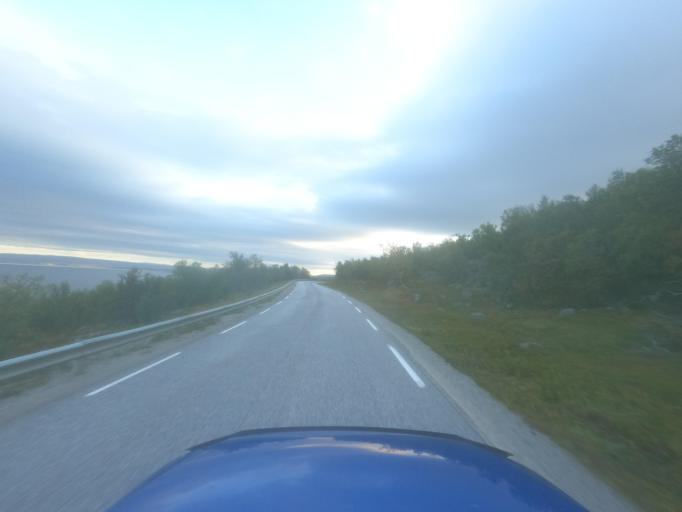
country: NO
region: Finnmark Fylke
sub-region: Porsanger
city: Lakselv
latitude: 70.3890
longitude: 25.1186
